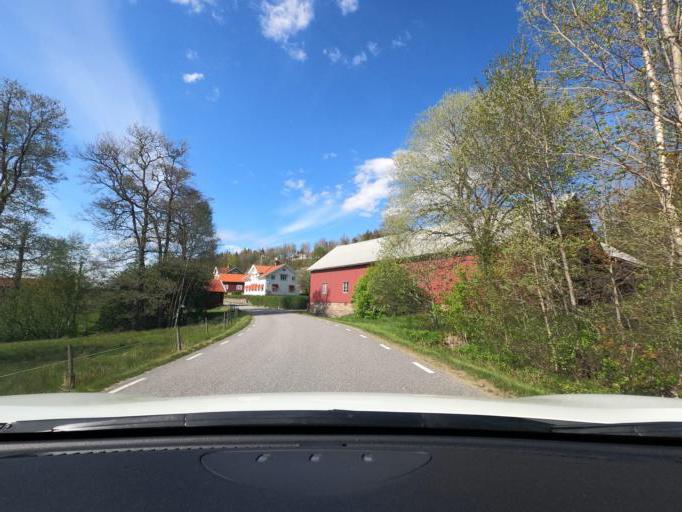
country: SE
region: Vaestra Goetaland
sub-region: Harryda Kommun
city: Ravlanda
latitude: 57.6344
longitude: 12.4991
